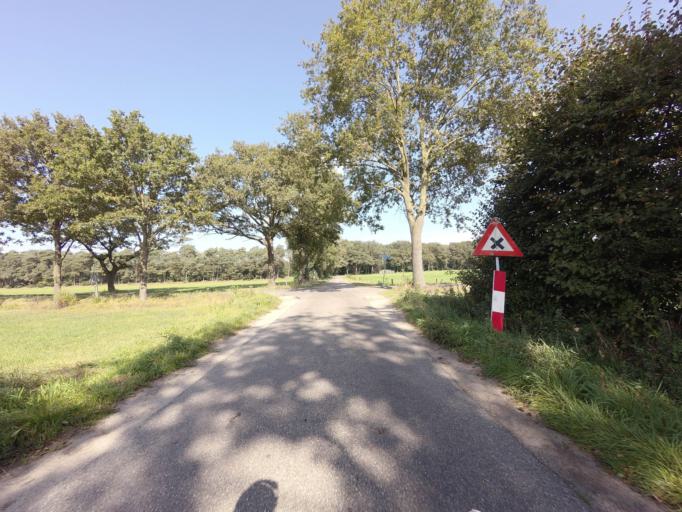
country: NL
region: Overijssel
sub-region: Gemeente Haaksbergen
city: Haaksbergen
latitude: 52.2054
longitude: 6.7751
